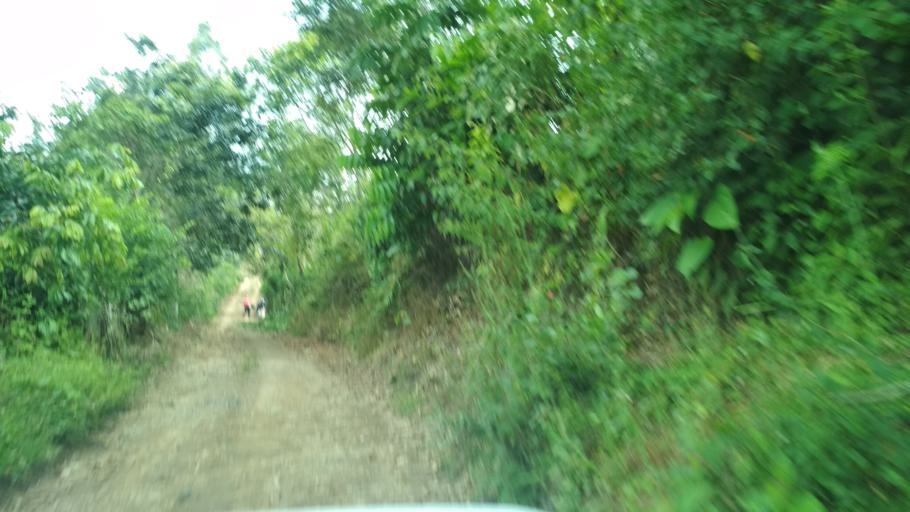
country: CO
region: Cauca
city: Lopez
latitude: 2.4023
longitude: -76.7132
